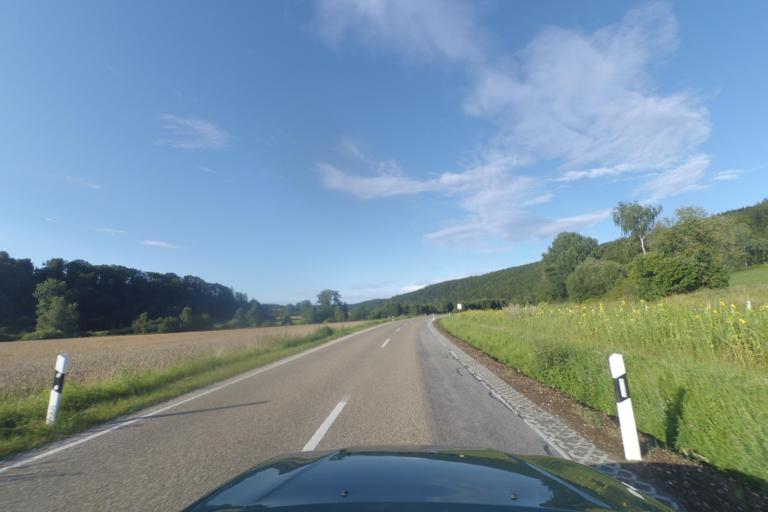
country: DE
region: Bavaria
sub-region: Upper Bavaria
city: Walting
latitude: 48.9025
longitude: 11.2932
